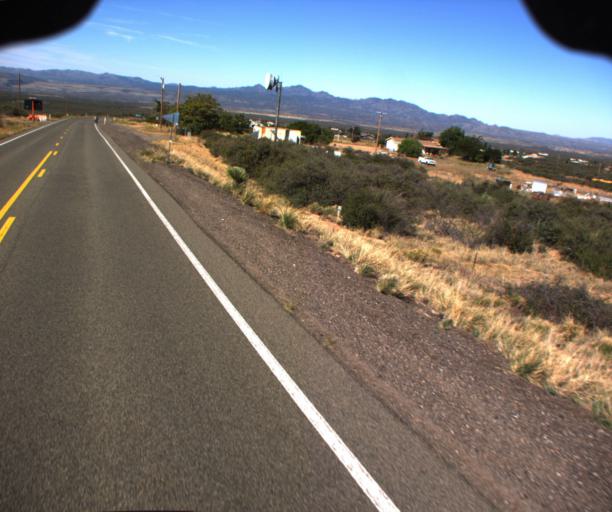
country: US
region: Arizona
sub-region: Yavapai County
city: Prescott
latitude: 34.4221
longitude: -112.5918
